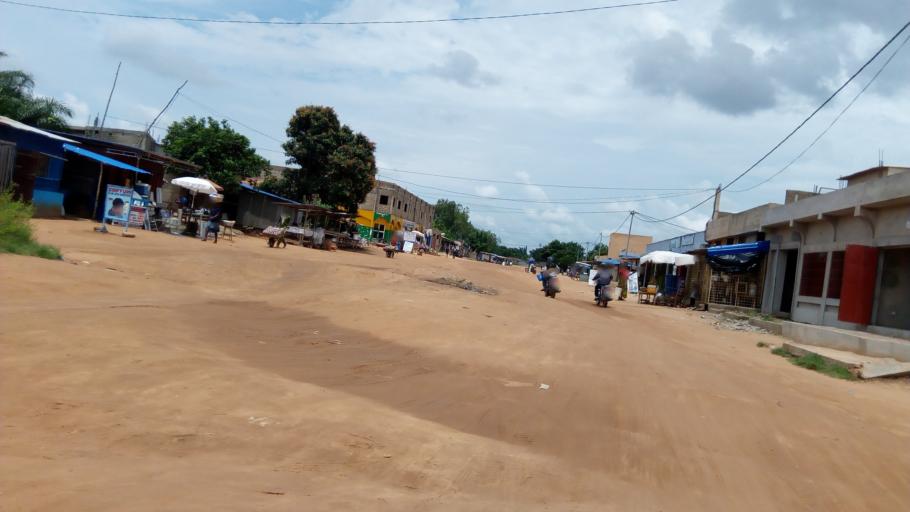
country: TG
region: Maritime
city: Lome
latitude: 6.2291
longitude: 1.1568
